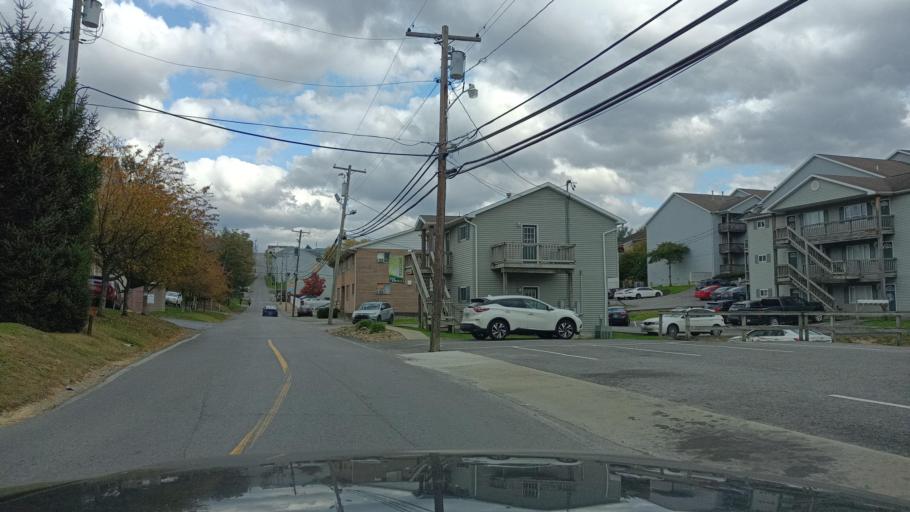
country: US
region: West Virginia
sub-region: Monongalia County
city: Morgantown
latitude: 39.6511
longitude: -79.9526
